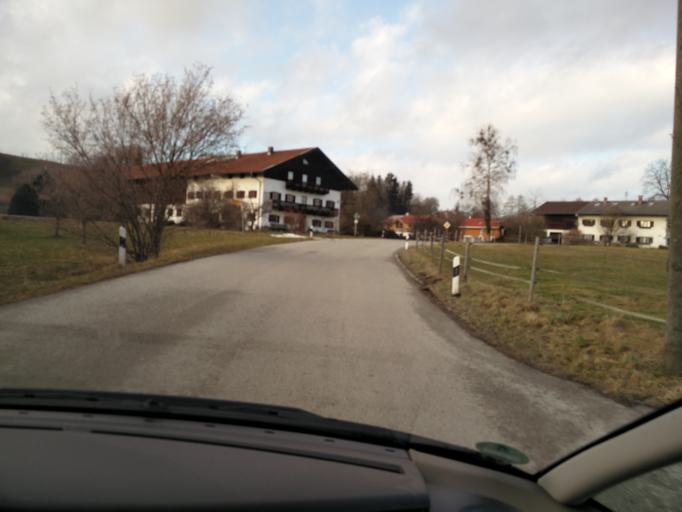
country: DE
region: Bavaria
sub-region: Upper Bavaria
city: Rimsting
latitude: 47.9083
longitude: 12.3355
